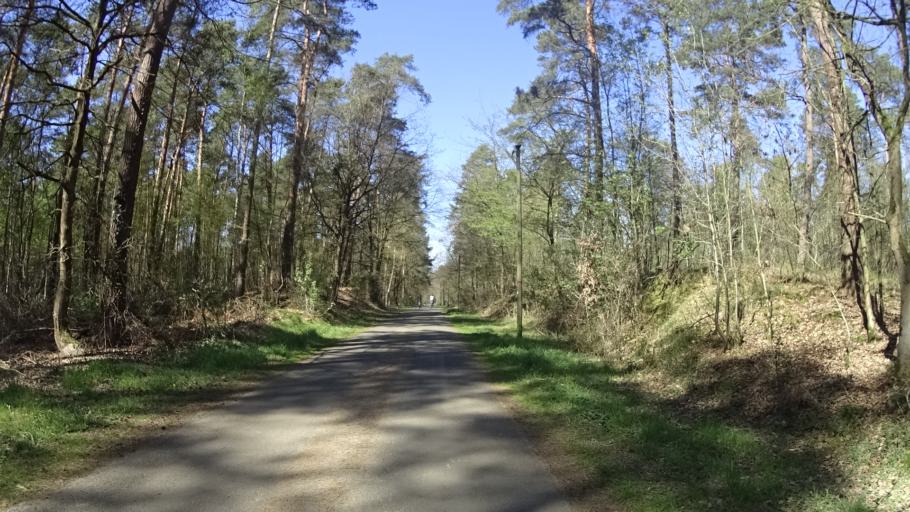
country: DE
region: North Rhine-Westphalia
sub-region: Regierungsbezirk Munster
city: Dulmen
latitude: 51.7847
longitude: 7.2655
